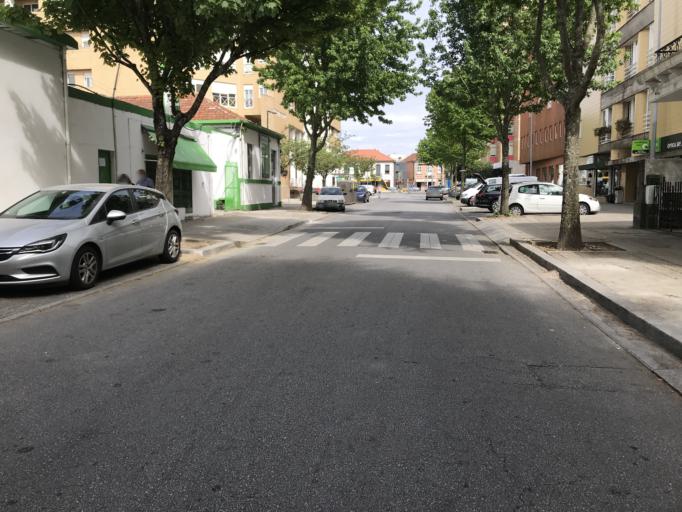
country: PT
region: Porto
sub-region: Matosinhos
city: Senhora da Hora
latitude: 41.1865
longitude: -8.6558
